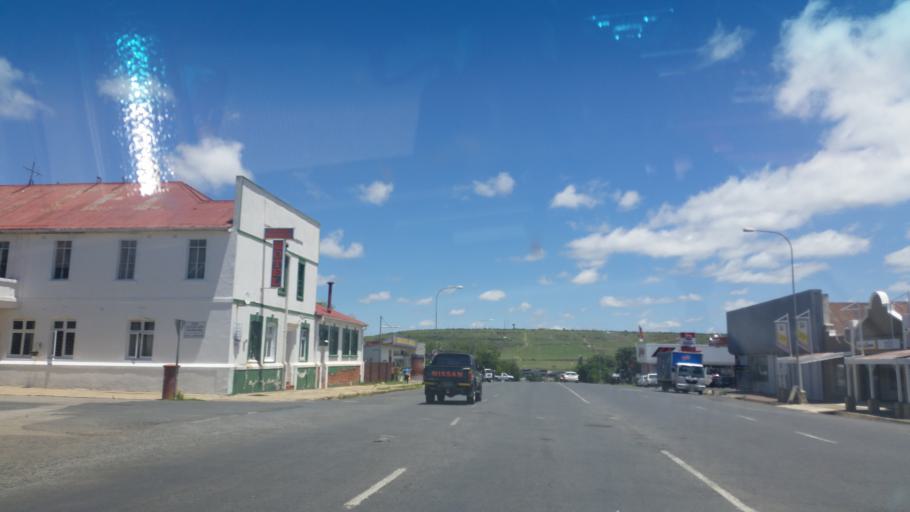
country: ZA
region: Orange Free State
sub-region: Thabo Mofutsanyana District Municipality
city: Harrismith
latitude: -28.2677
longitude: 29.1227
